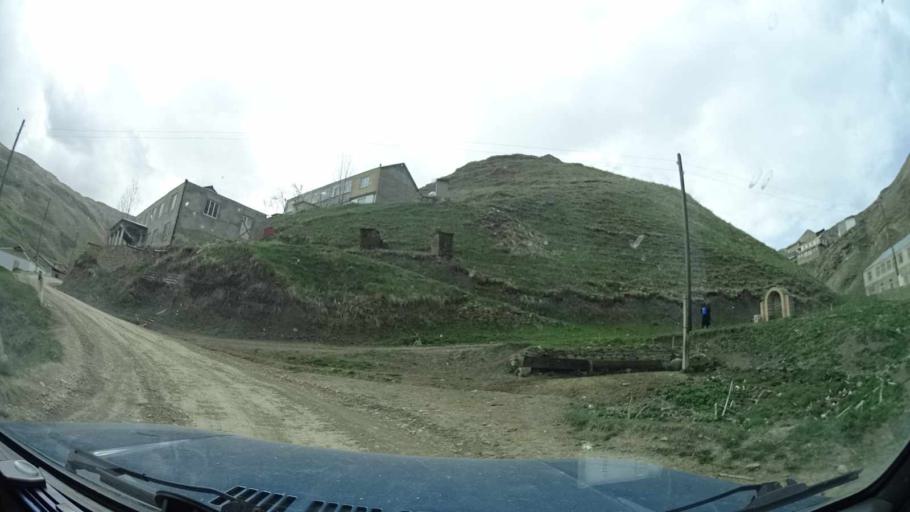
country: RU
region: Dagestan
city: Usisha
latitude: 42.1350
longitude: 47.3644
